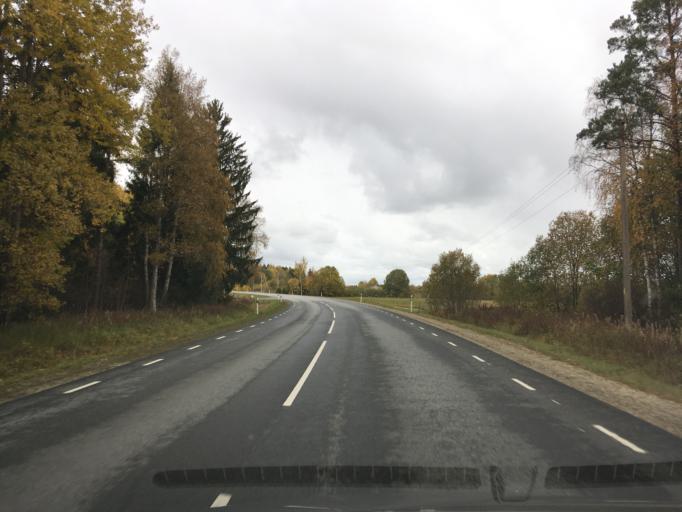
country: EE
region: Harju
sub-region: Anija vald
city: Kehra
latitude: 59.3192
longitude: 25.3433
